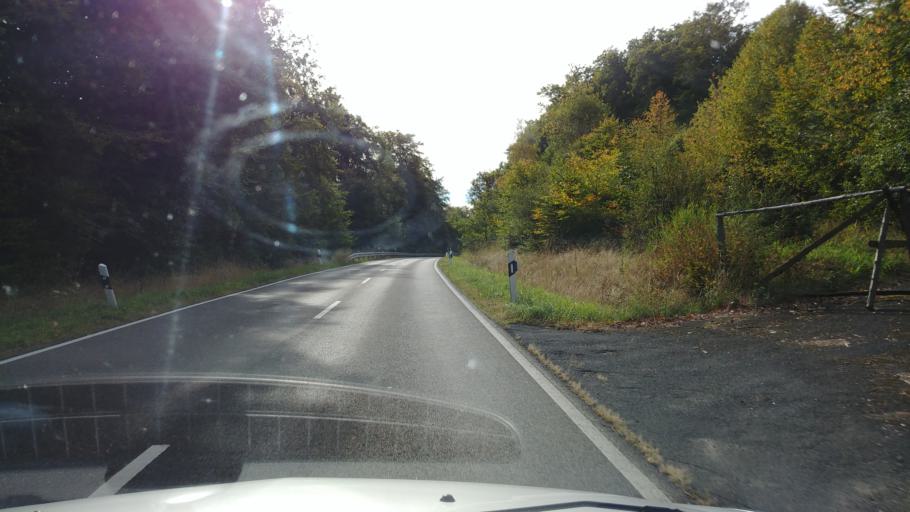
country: DE
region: Hesse
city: Taunusstein
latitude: 50.1852
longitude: 8.1436
